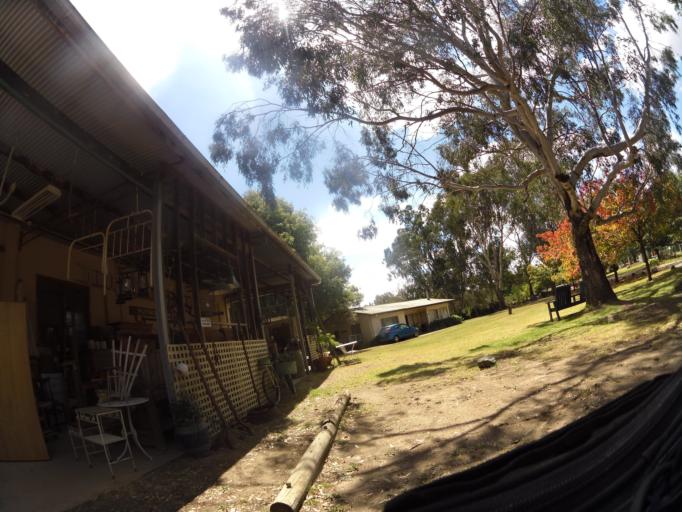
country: AU
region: Victoria
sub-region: Benalla
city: Benalla
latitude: -36.7465
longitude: 146.0119
